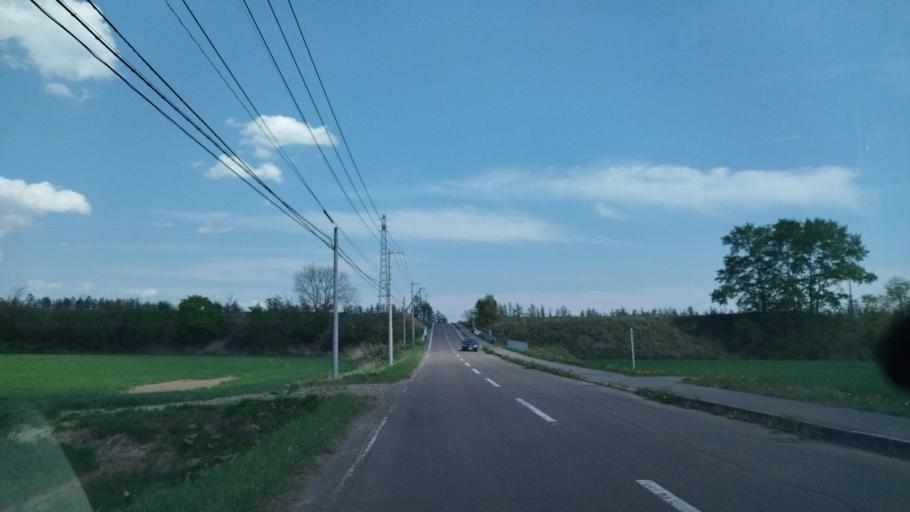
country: JP
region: Hokkaido
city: Otofuke
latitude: 43.1011
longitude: 143.2191
